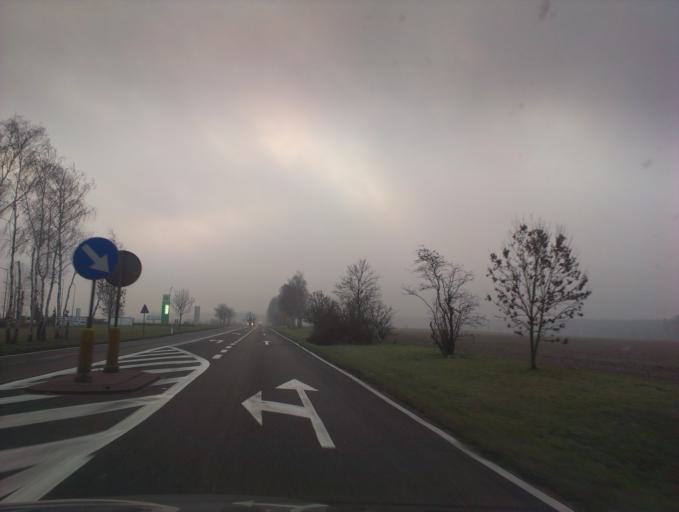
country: PL
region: Greater Poland Voivodeship
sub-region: Powiat chodzieski
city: Chodziez
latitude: 52.9491
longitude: 16.9447
